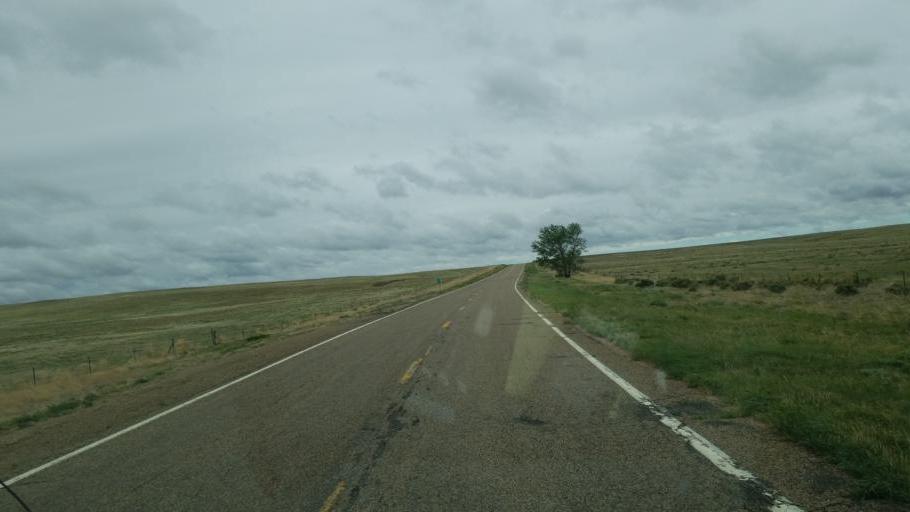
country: US
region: Colorado
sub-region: Lincoln County
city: Hugo
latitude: 38.8491
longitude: -103.4881
